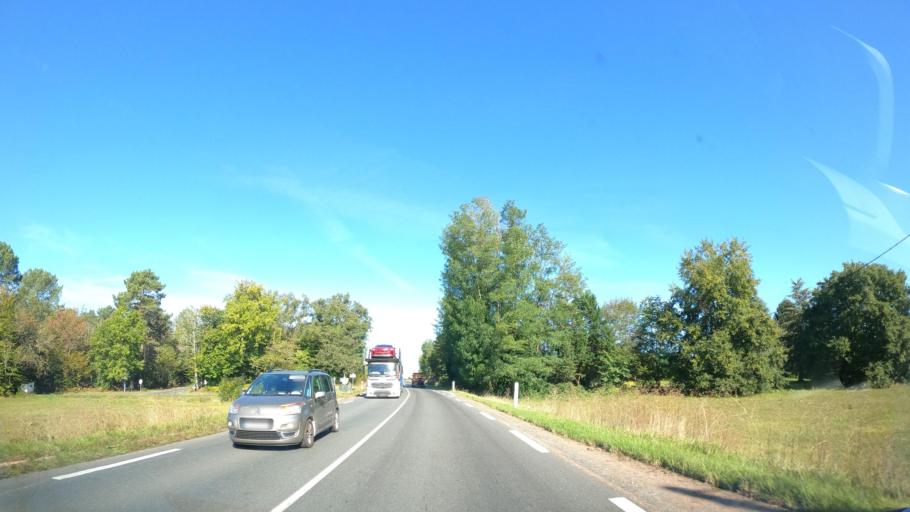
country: FR
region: Aquitaine
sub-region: Departement de la Dordogne
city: Notre-Dame-de-Sanilhac
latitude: 45.1002
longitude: 0.6954
